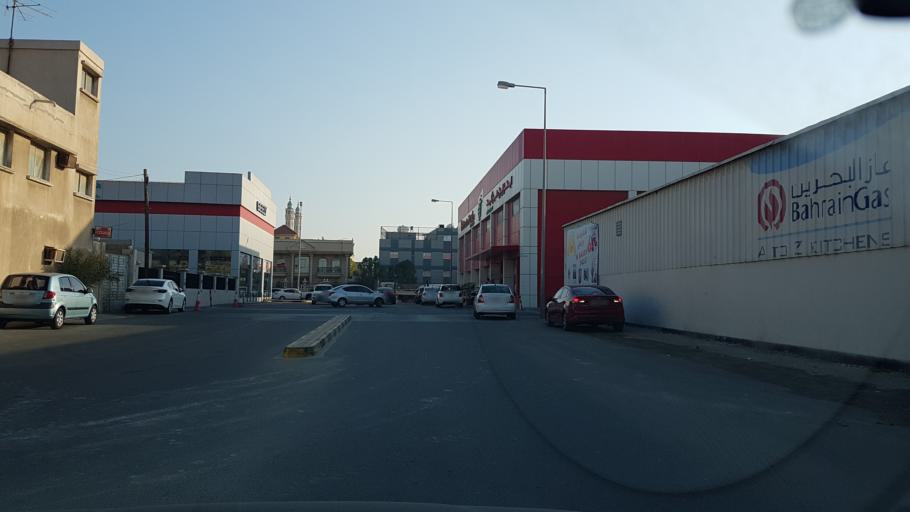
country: BH
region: Northern
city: Madinat `Isa
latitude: 26.1877
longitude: 50.5381
